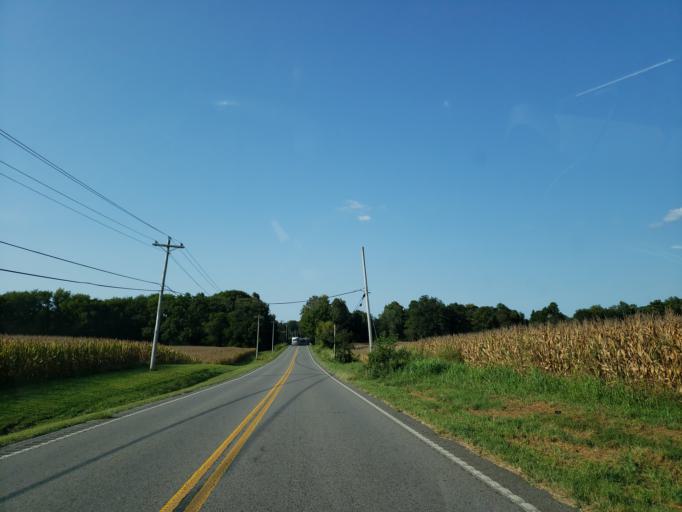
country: US
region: Tennessee
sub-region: Bradley County
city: Wildwood Lake
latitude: 35.0066
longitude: -84.7341
